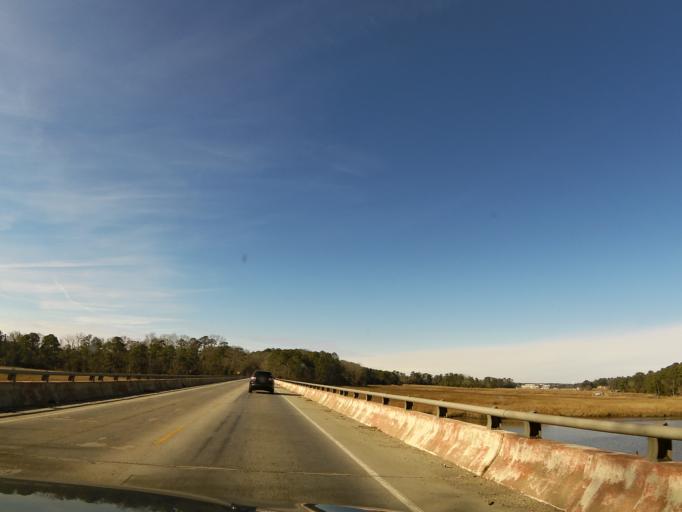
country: US
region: Virginia
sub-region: Isle of Wight County
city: Smithfield
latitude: 36.9649
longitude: -76.6125
